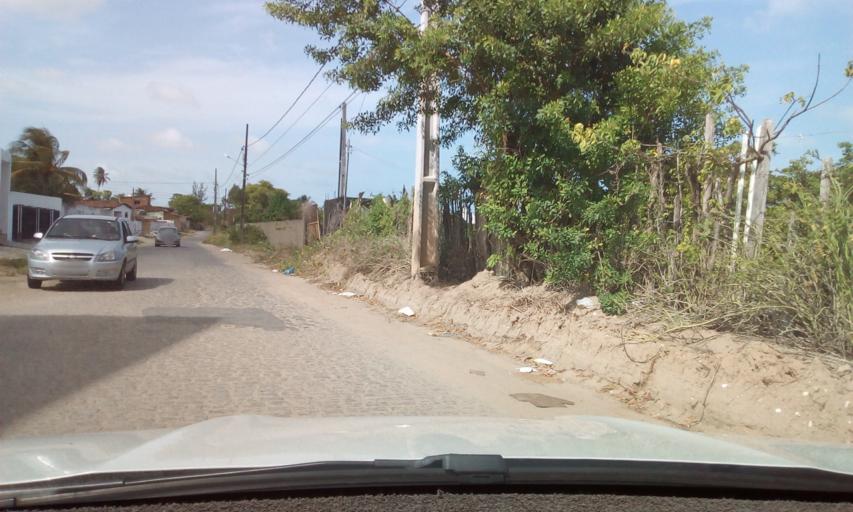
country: BR
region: Paraiba
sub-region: Joao Pessoa
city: Joao Pessoa
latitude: -7.1590
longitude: -34.8460
